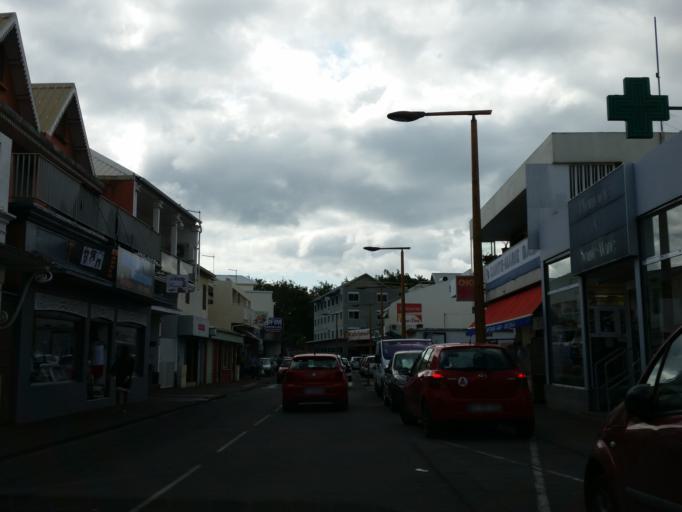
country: RE
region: Reunion
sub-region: Reunion
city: Sainte-Marie
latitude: -20.8971
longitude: 55.5500
